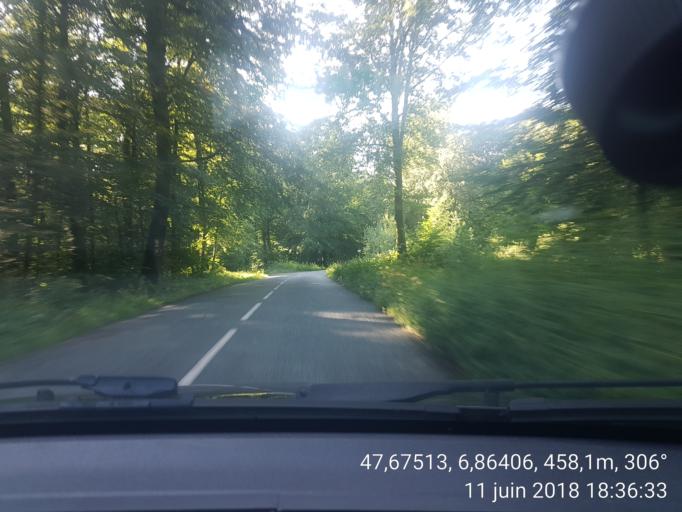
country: FR
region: Franche-Comte
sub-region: Territoire de Belfort
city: Offemont
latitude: 47.6750
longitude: 6.8642
